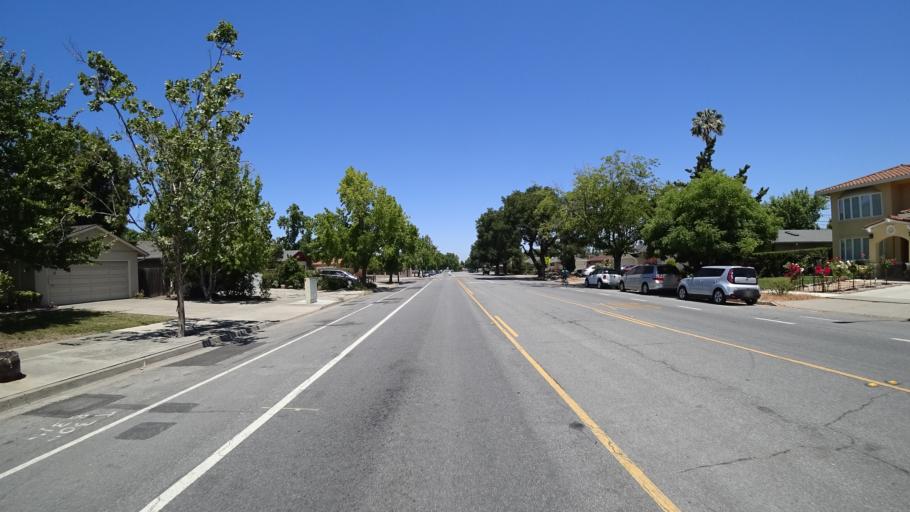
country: US
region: California
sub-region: Santa Clara County
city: Cupertino
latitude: 37.3032
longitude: -122.0151
